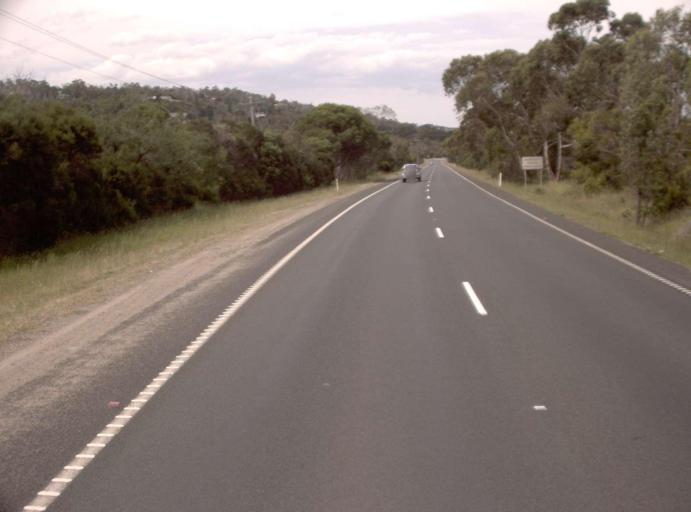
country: AU
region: Victoria
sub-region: Mornington Peninsula
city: Moorooduc
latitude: -38.2095
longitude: 145.1116
